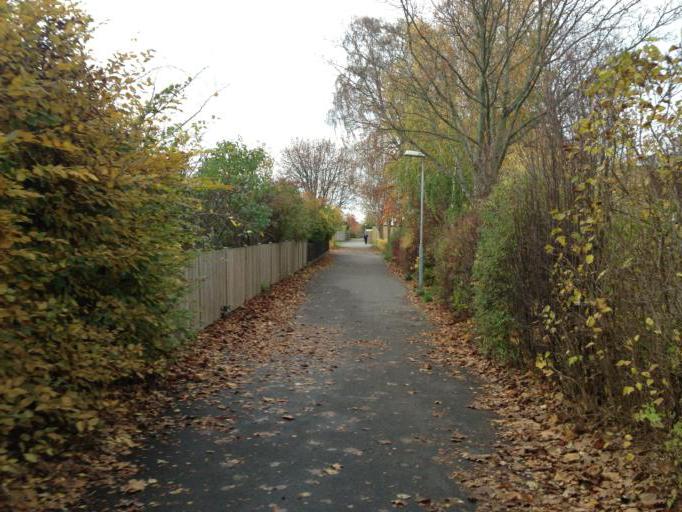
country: SE
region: Skane
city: Bjarred
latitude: 55.7270
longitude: 13.0156
